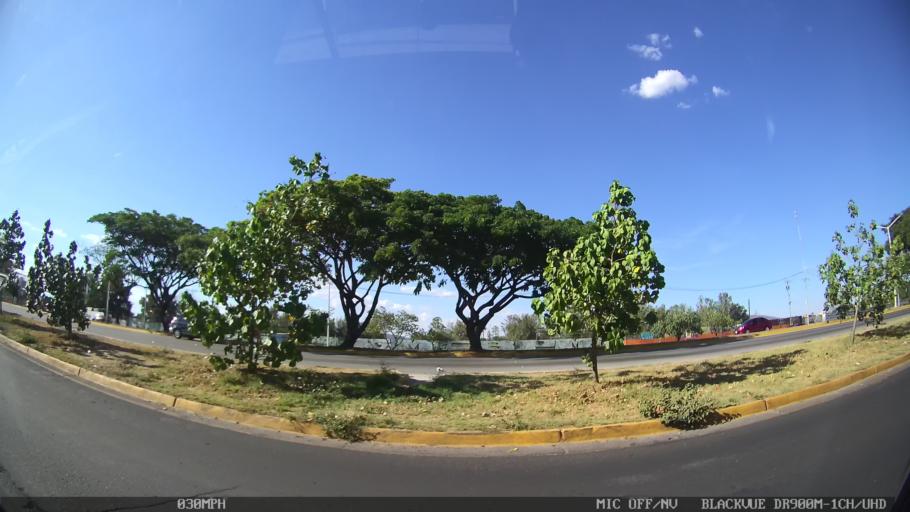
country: MX
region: Jalisco
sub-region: Zapopan
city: Zapopan
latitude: 20.7181
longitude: -103.3117
